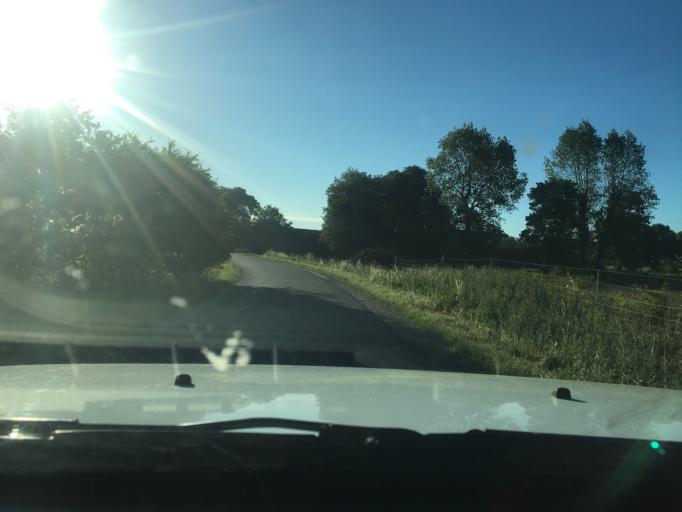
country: DK
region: Central Jutland
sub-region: Randers Kommune
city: Randers
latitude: 56.4109
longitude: 10.0526
